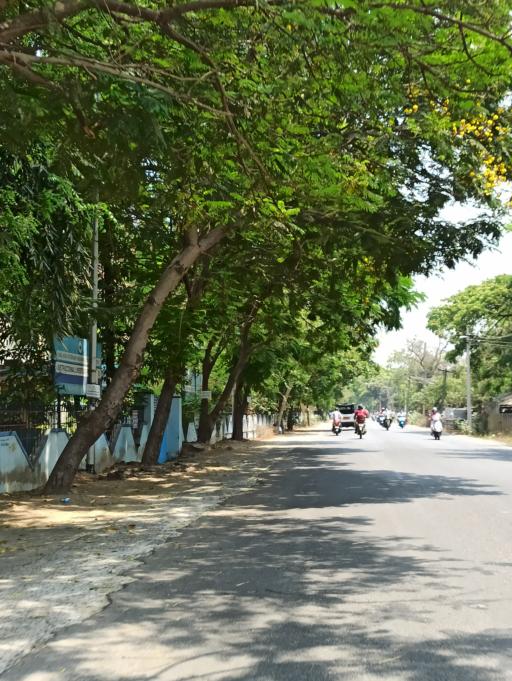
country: IN
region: Tamil Nadu
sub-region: Thiruvallur
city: Chinnasekkadu
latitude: 13.1611
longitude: 80.2438
